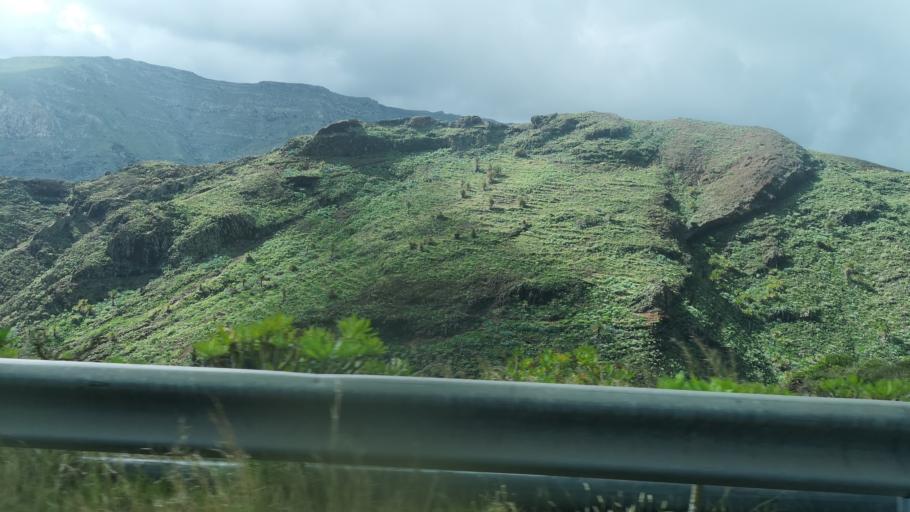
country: ES
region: Canary Islands
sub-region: Provincia de Santa Cruz de Tenerife
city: San Sebastian de la Gomera
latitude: 28.1196
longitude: -17.1433
